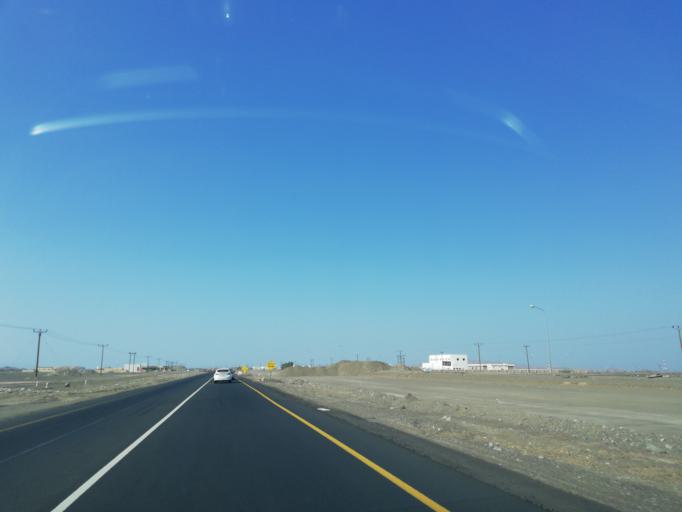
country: OM
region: Ash Sharqiyah
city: Ibra'
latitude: 22.7075
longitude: 58.1427
